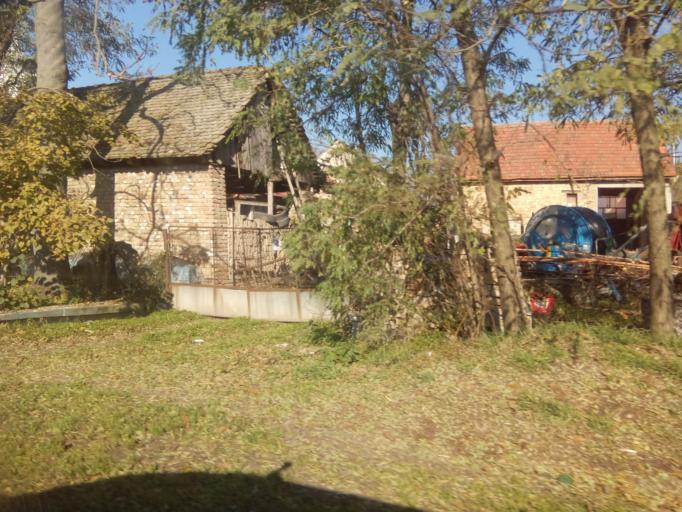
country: RS
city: Glozan
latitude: 45.2746
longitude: 19.5711
